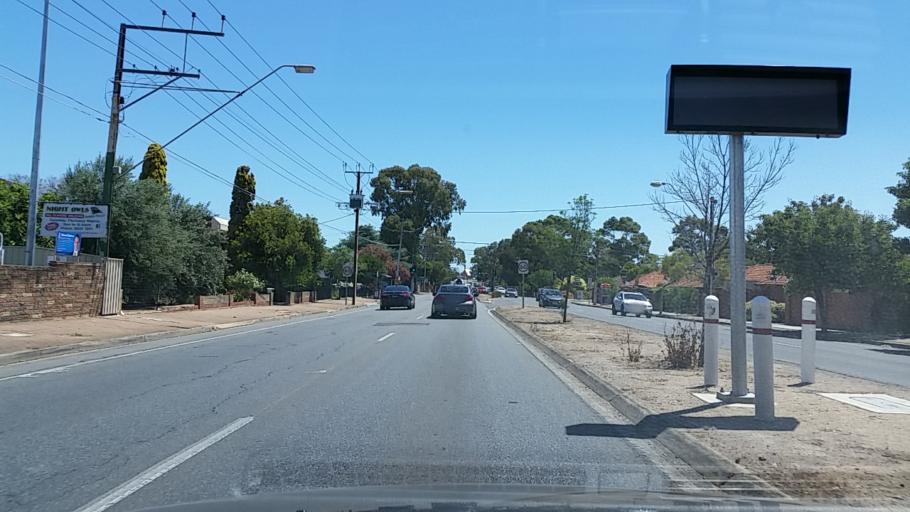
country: AU
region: South Australia
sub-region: Norwood Payneham St Peters
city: Payneham
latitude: -34.8933
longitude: 138.6468
